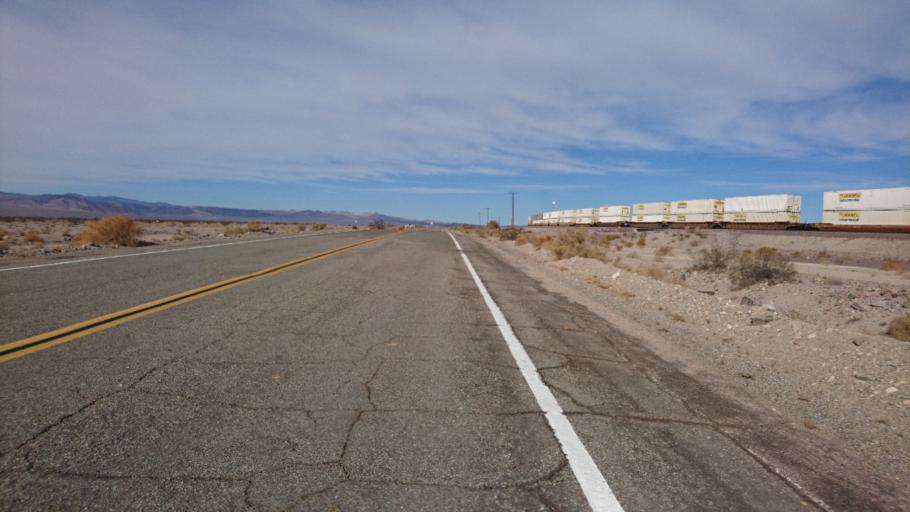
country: US
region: California
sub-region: San Bernardino County
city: Twentynine Palms
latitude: 34.6022
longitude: -115.9539
